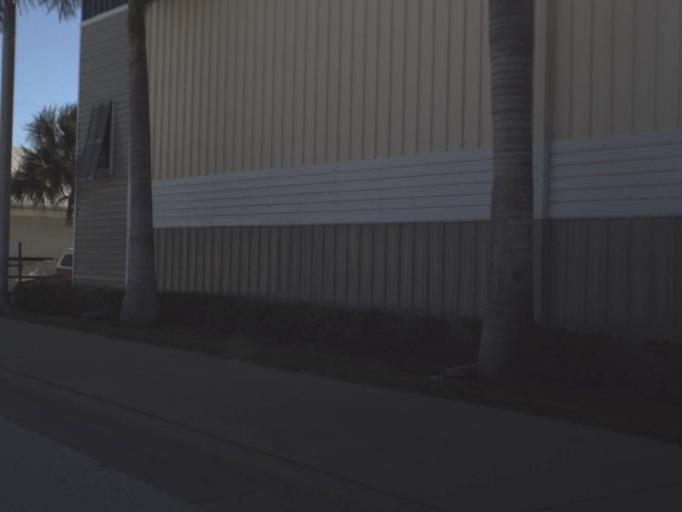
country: US
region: Florida
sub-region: Sarasota County
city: Englewood
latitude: 26.9456
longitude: -82.3524
